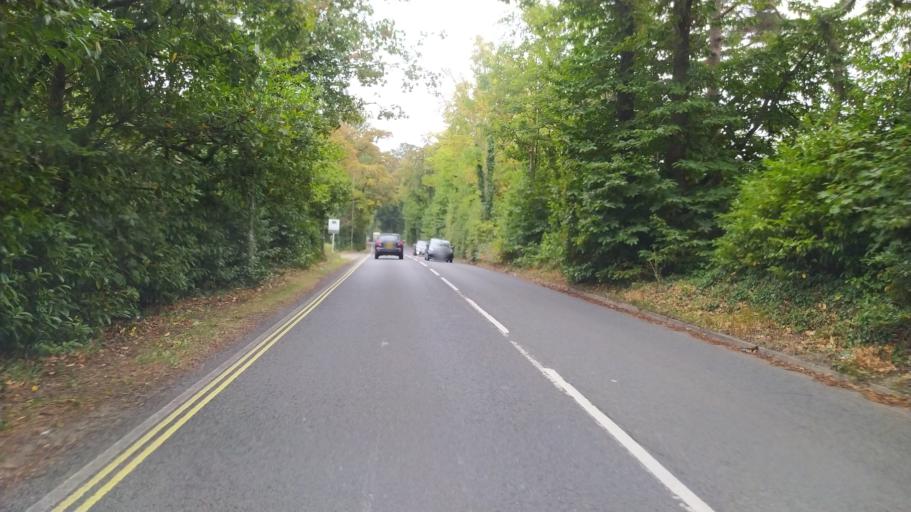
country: GB
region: England
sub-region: Hampshire
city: West End
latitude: 50.9170
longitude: -1.3303
